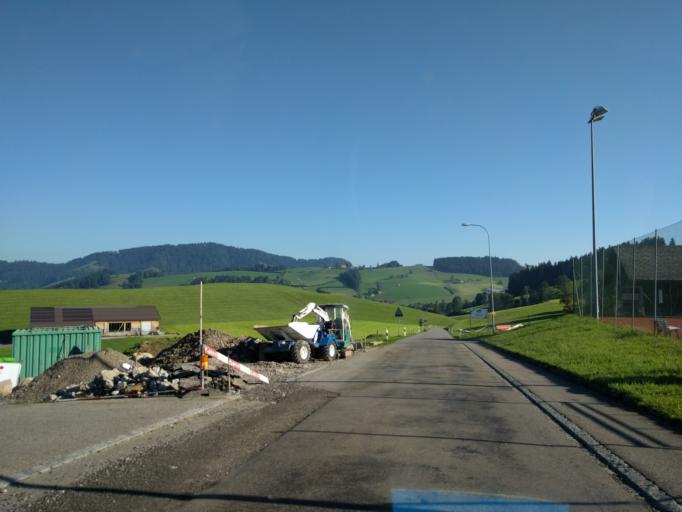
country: CH
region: Saint Gallen
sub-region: Wahlkreis Toggenburg
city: Sankt Peterzell
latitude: 47.3075
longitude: 9.1955
